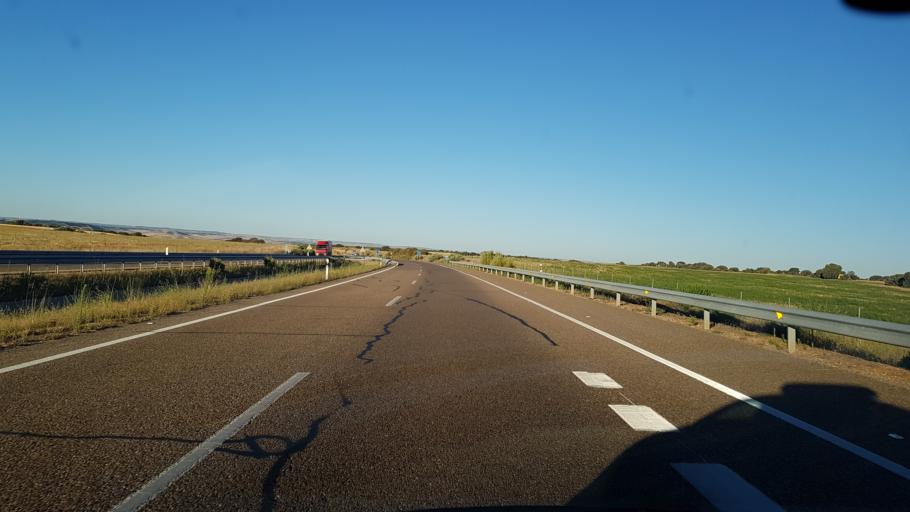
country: ES
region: Castille and Leon
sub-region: Provincia de Zamora
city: Matilla la Seca
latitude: 41.5622
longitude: -5.5283
